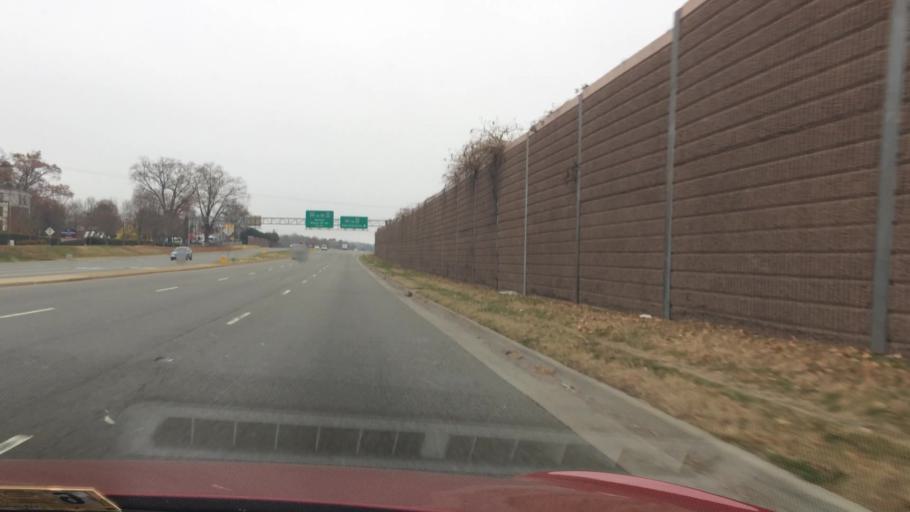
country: US
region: Virginia
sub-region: Henrico County
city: Glen Allen
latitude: 37.6658
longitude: -77.4607
